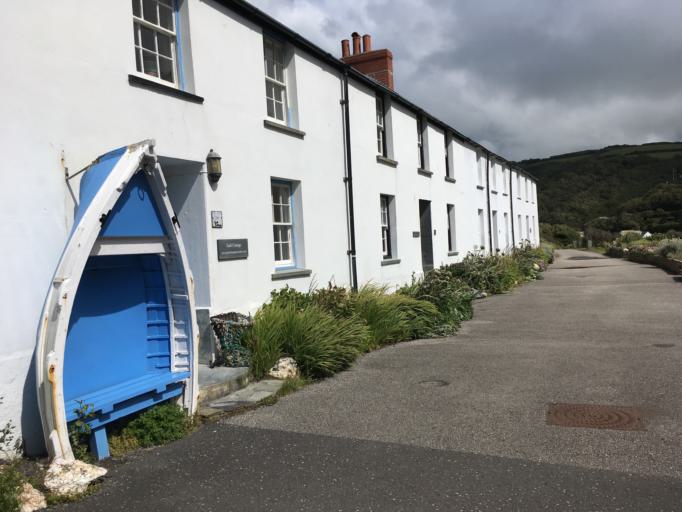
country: GB
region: England
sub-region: Cornwall
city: Tintagel
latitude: 50.6913
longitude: -4.6966
